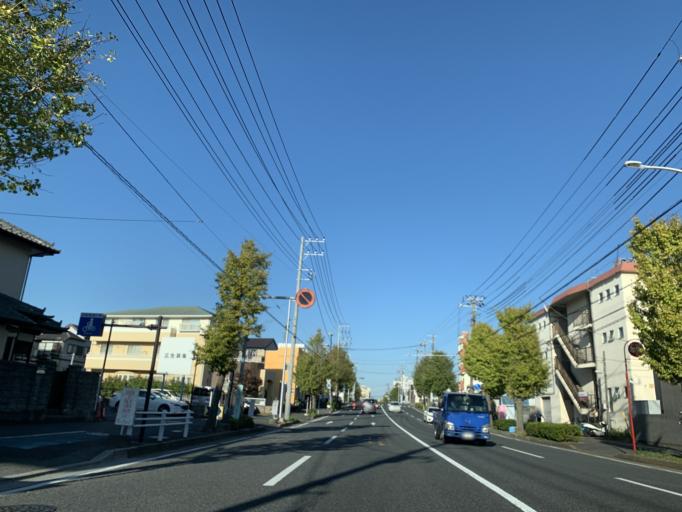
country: JP
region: Tokyo
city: Urayasu
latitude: 35.6581
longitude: 139.8960
